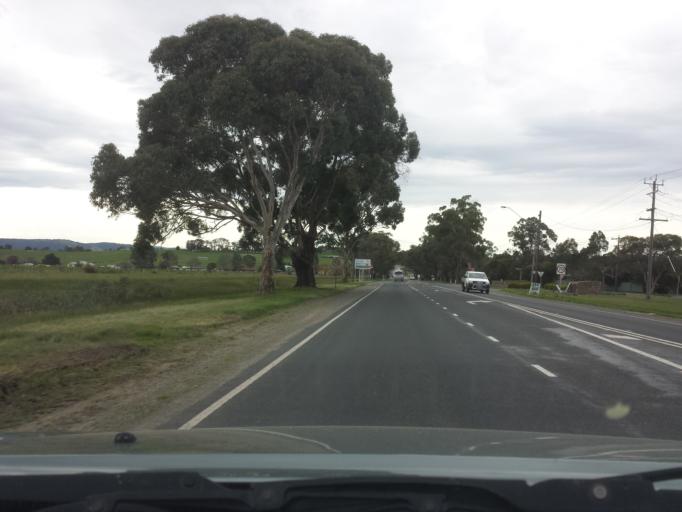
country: AU
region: Victoria
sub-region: Yarra Ranges
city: Lilydale
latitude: -37.7297
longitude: 145.3775
